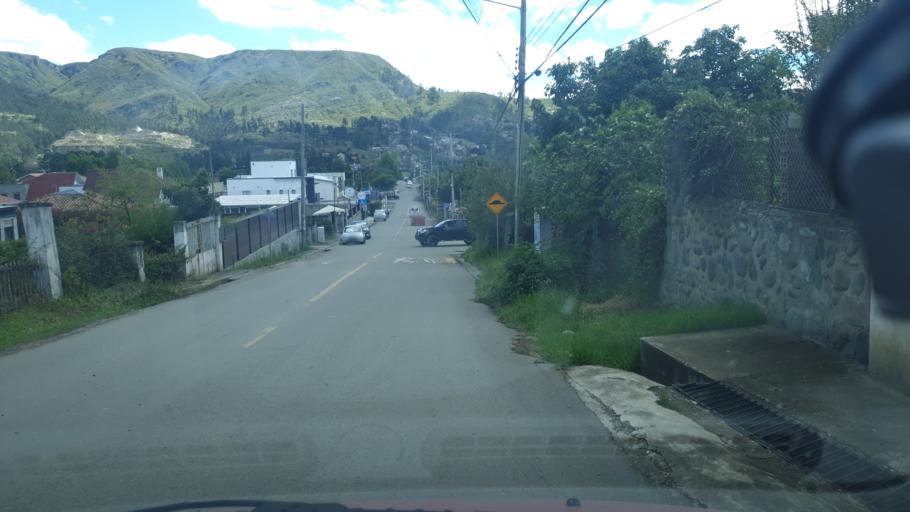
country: EC
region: Azuay
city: Llacao
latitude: -2.8558
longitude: -78.9100
